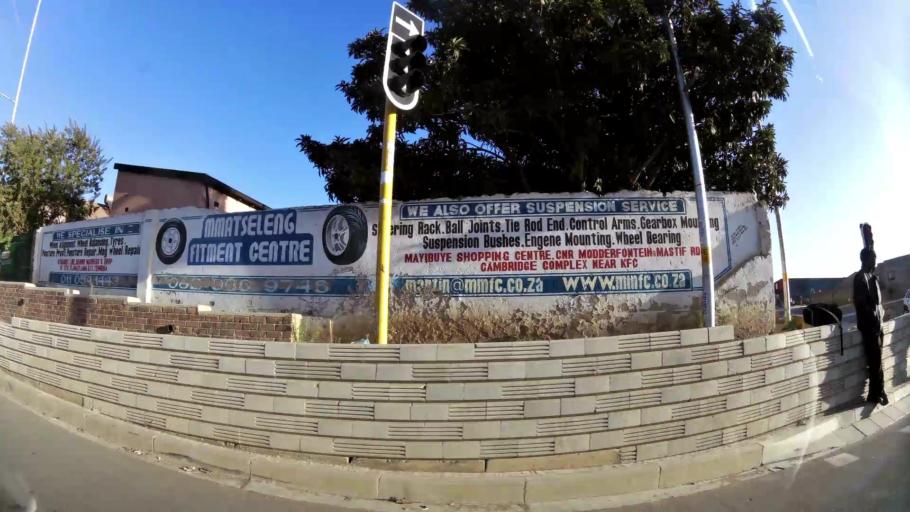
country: ZA
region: Gauteng
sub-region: Ekurhuleni Metropolitan Municipality
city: Tembisa
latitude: -26.0169
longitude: 28.2120
